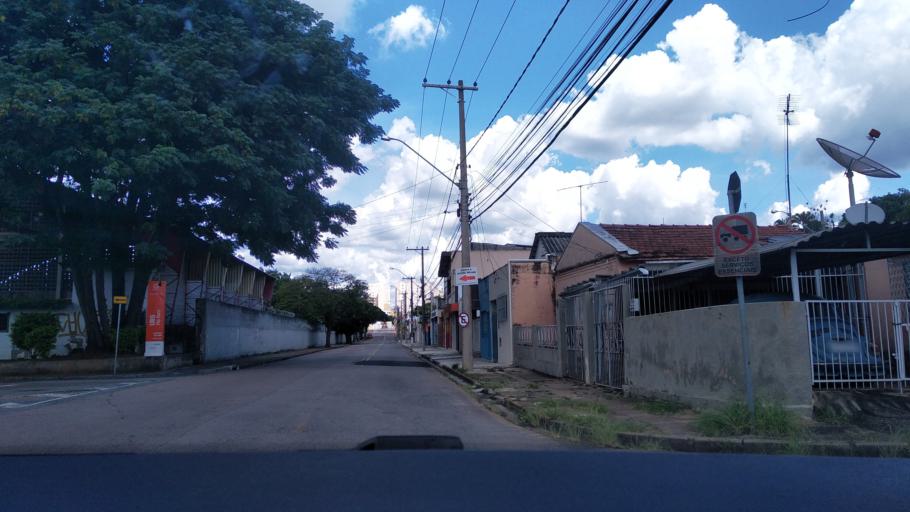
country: BR
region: Sao Paulo
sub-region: Jundiai
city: Jundiai
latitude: -23.2121
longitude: -46.8777
